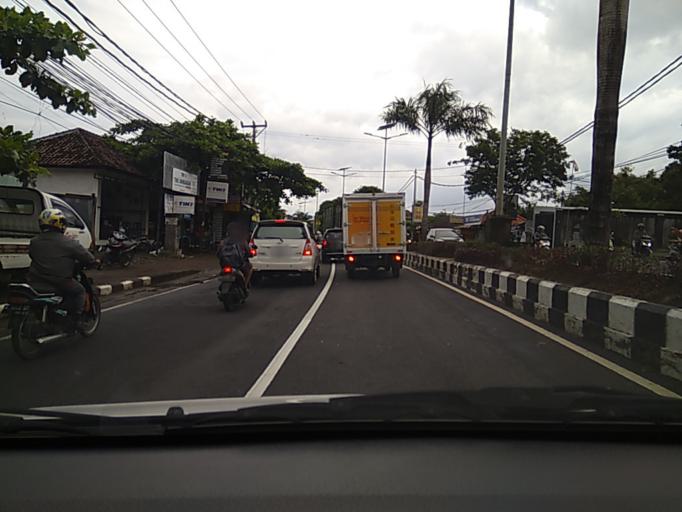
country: ID
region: Bali
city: Jimbaran
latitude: -8.7840
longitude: 115.1894
